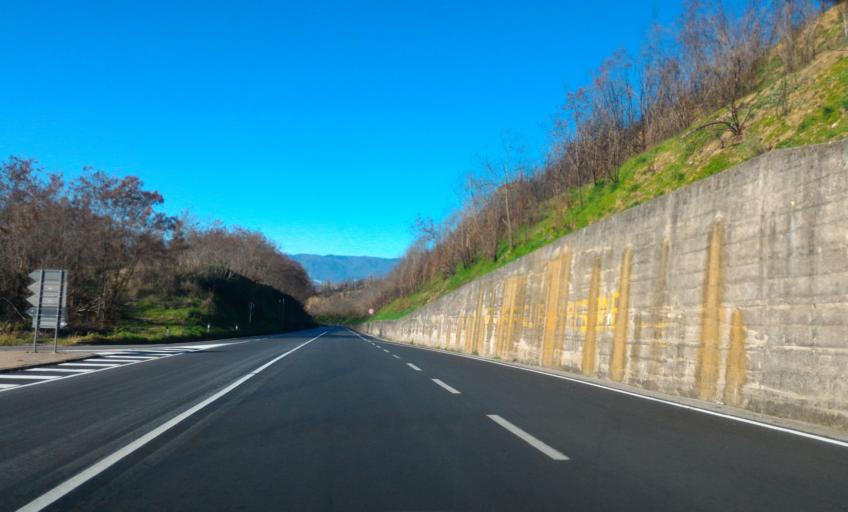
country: IT
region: Calabria
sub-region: Provincia di Cosenza
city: Rovito
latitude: 39.2970
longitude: 16.3032
